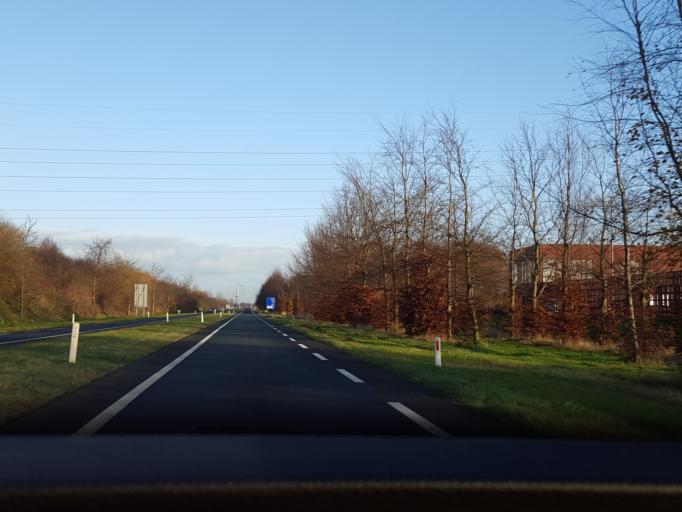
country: NL
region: Gelderland
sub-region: Gemeente Zutphen
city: Leesten
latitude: 52.1223
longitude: 6.2221
